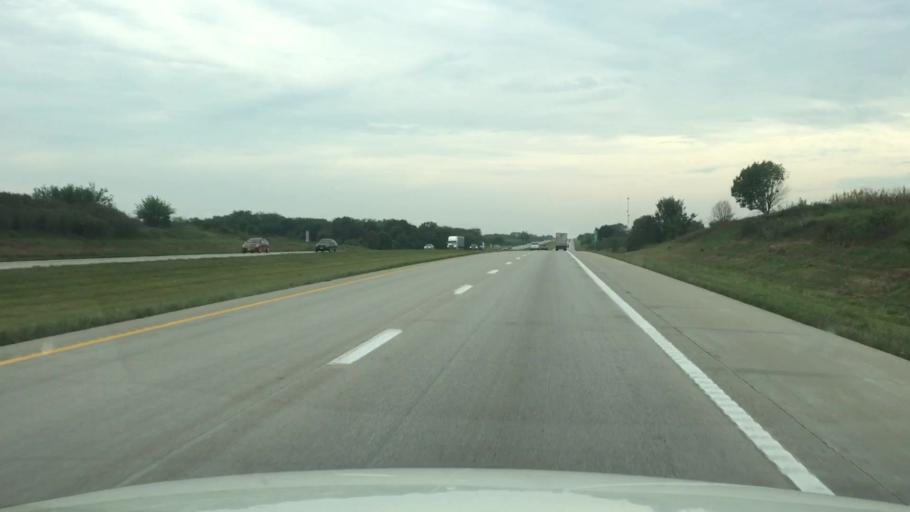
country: US
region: Missouri
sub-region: Clinton County
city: Cameron
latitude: 39.6288
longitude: -94.2457
